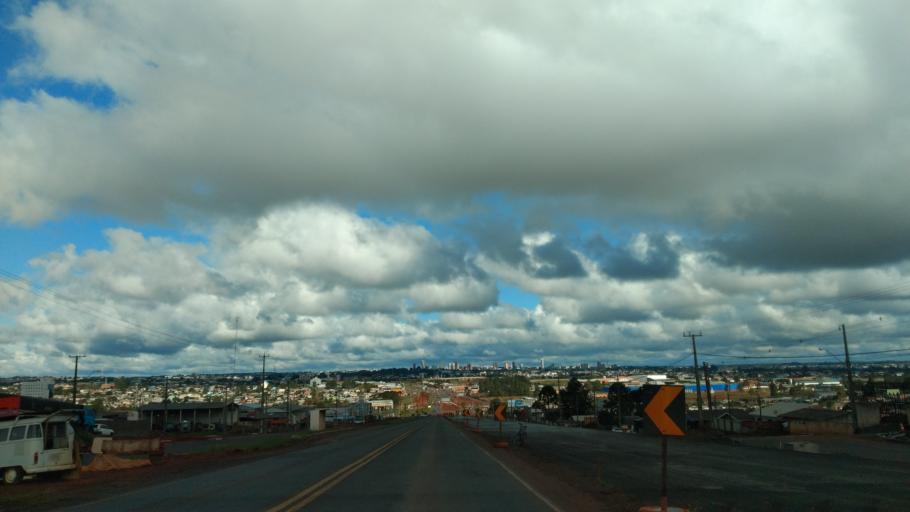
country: BR
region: Parana
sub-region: Guarapuava
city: Guarapuava
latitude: -25.3465
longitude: -51.4894
